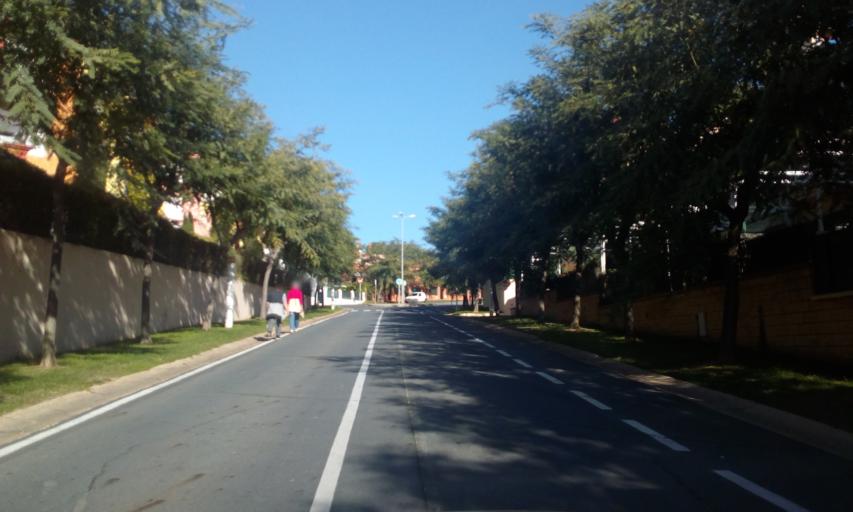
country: ES
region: Andalusia
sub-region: Provincia de Huelva
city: Lepe
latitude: 37.2094
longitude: -7.2437
